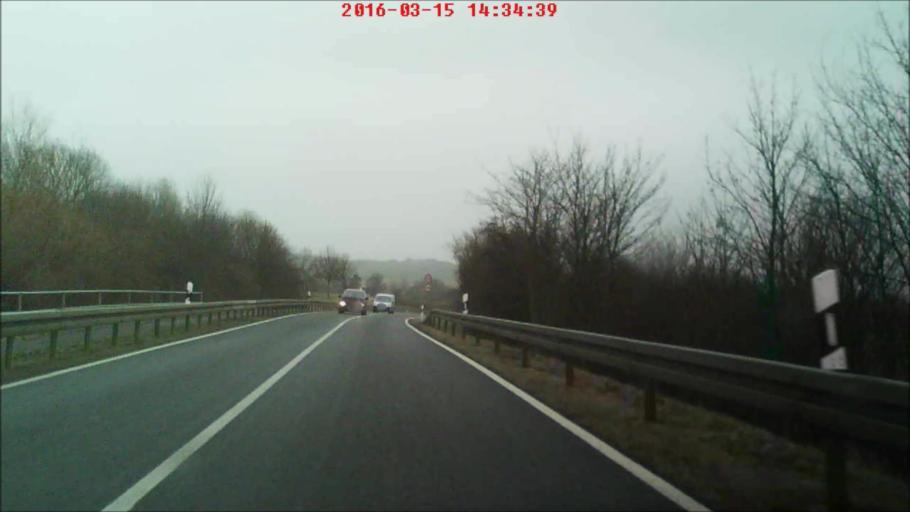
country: DE
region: Thuringia
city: Rockhausen
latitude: 50.9094
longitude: 11.0571
